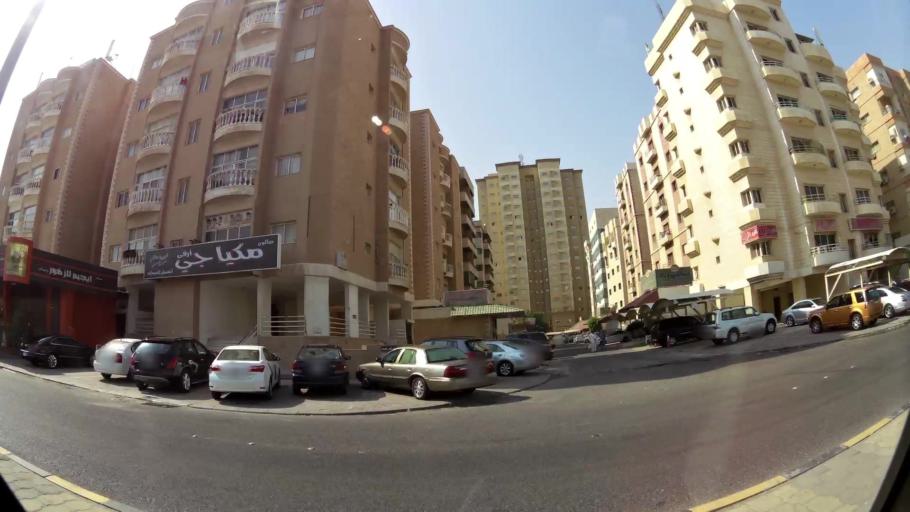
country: KW
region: Muhafazat Hawalli
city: Hawalli
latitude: 29.3432
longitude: 48.0219
